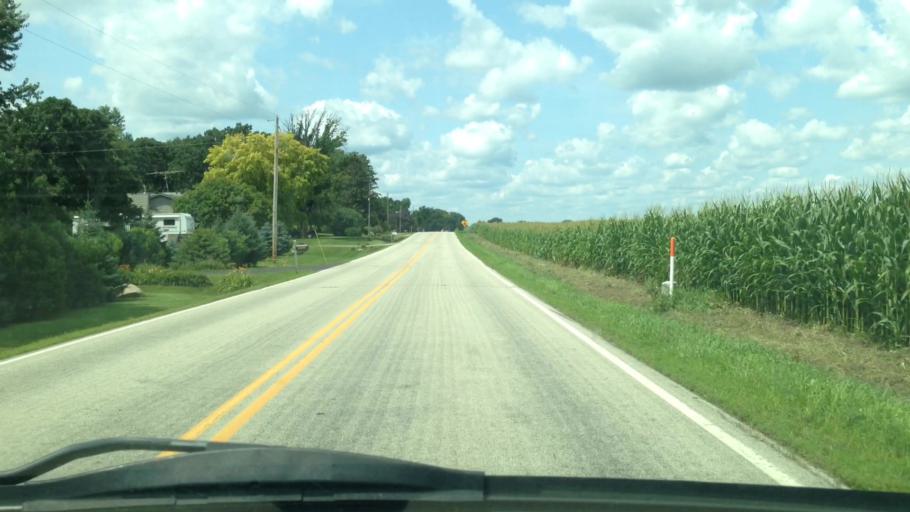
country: US
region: Minnesota
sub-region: Olmsted County
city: Rochester
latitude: 43.9532
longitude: -92.5137
